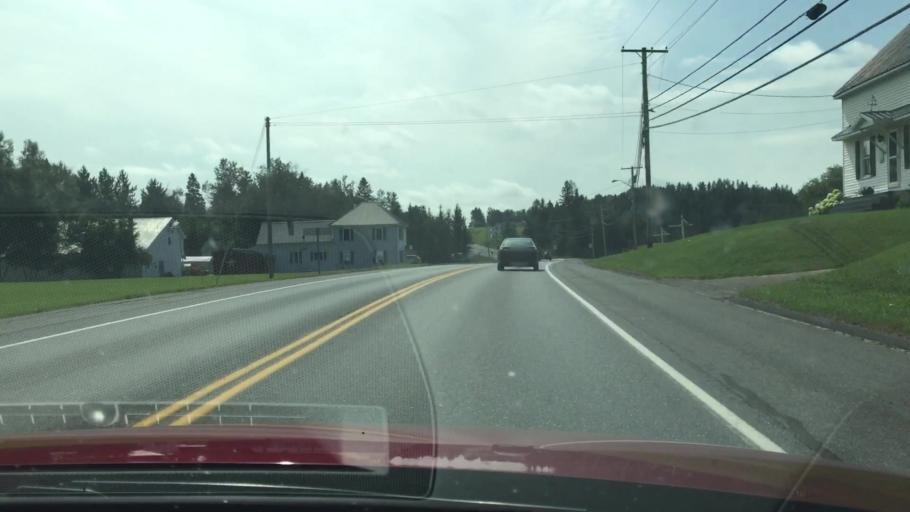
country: CA
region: New Brunswick
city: Florenceville-Bristol
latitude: 46.4193
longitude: -67.8435
